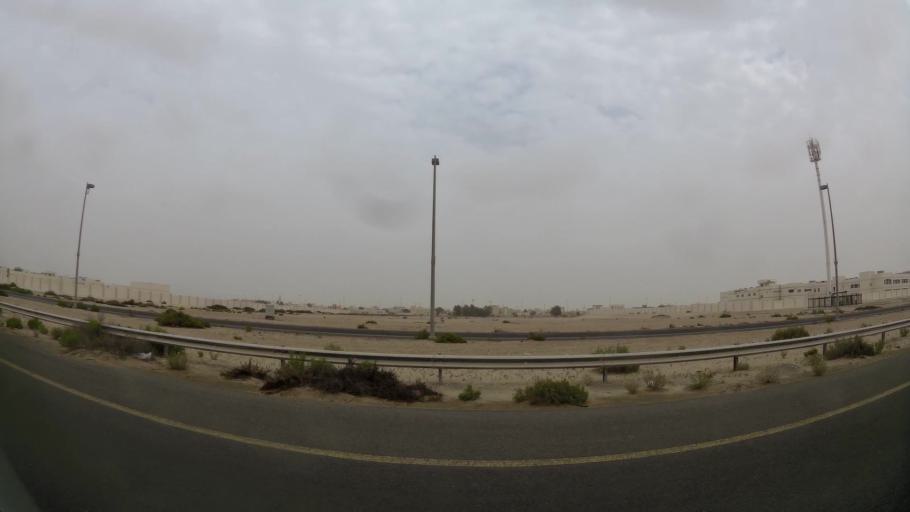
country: AE
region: Abu Dhabi
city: Abu Dhabi
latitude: 24.3920
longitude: 54.7344
